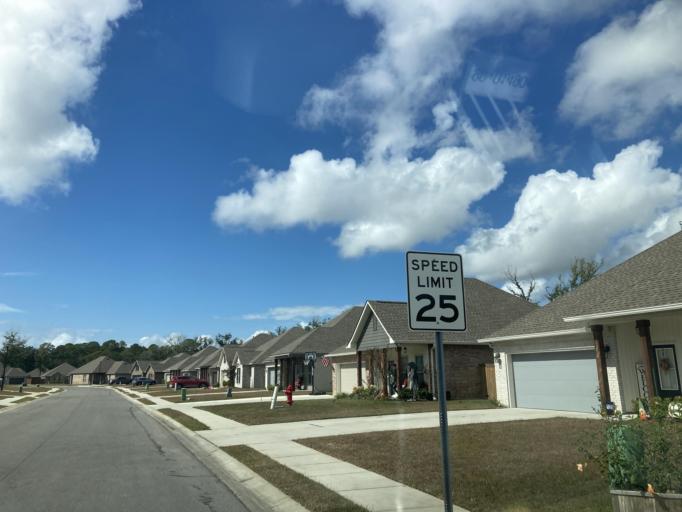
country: US
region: Mississippi
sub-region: Jackson County
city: Gulf Hills
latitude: 30.4521
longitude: -88.8307
